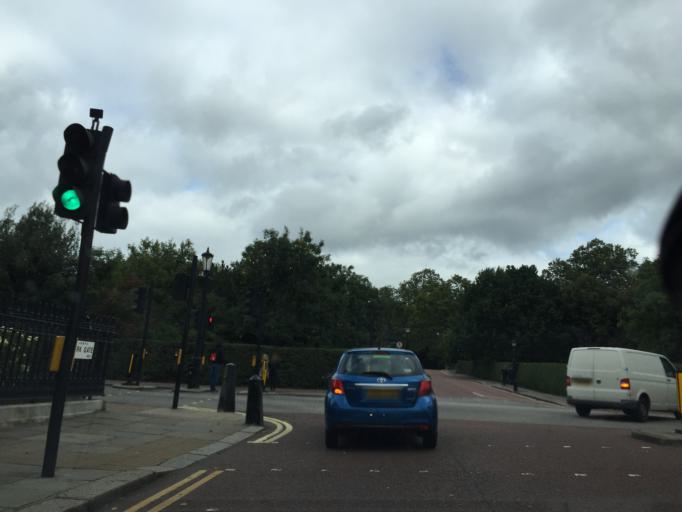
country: GB
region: England
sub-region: Greater London
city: Camden Town
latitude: 51.5238
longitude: -0.1529
